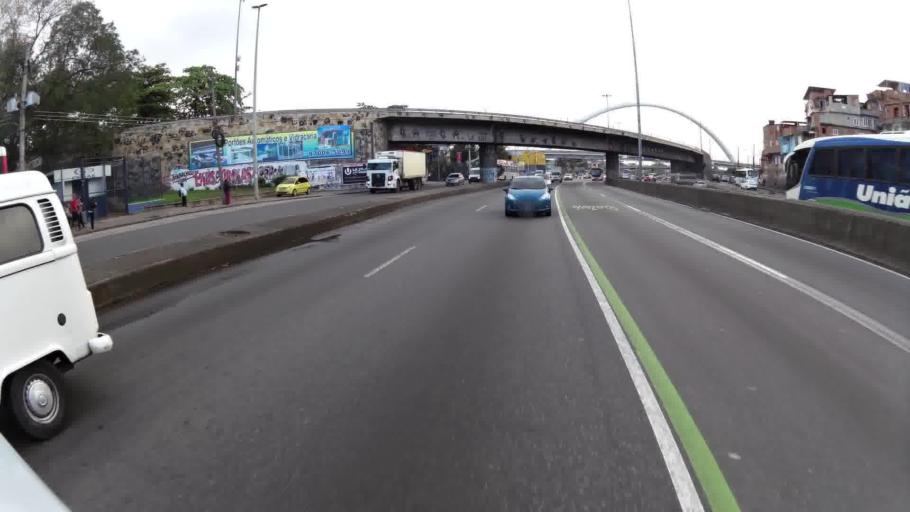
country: BR
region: Rio de Janeiro
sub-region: Rio De Janeiro
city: Rio de Janeiro
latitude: -22.8475
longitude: -43.2473
